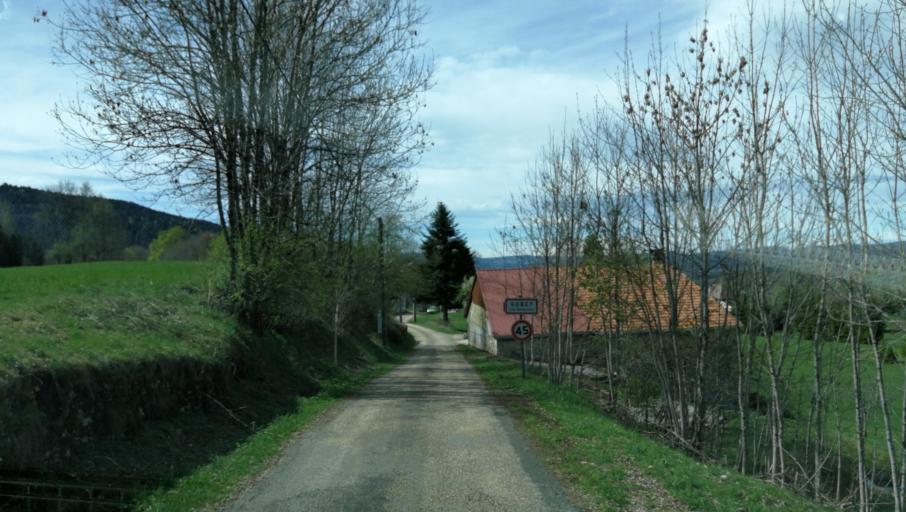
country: FR
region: Rhone-Alpes
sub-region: Departement de l'Ain
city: Chatillon-en-Michaille
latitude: 46.2560
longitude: 5.7885
